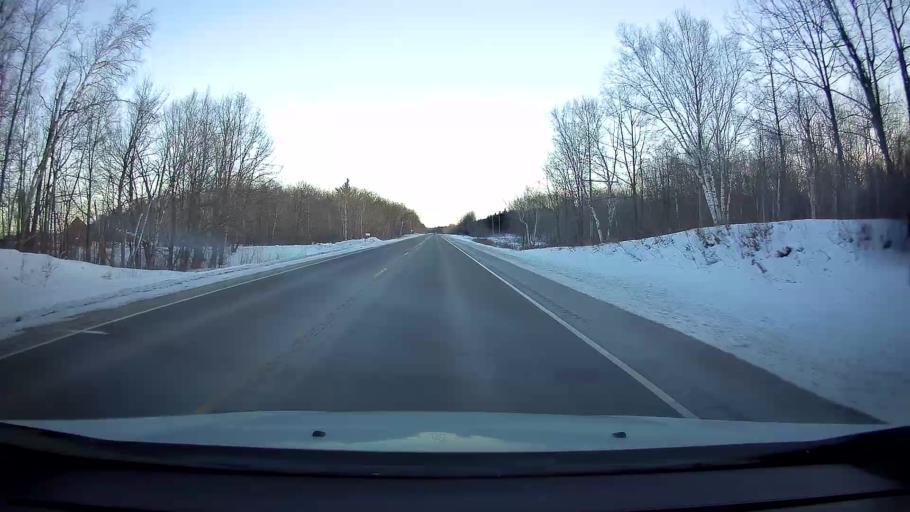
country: US
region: Wisconsin
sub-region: Washburn County
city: Shell Lake
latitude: 45.6974
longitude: -91.9611
